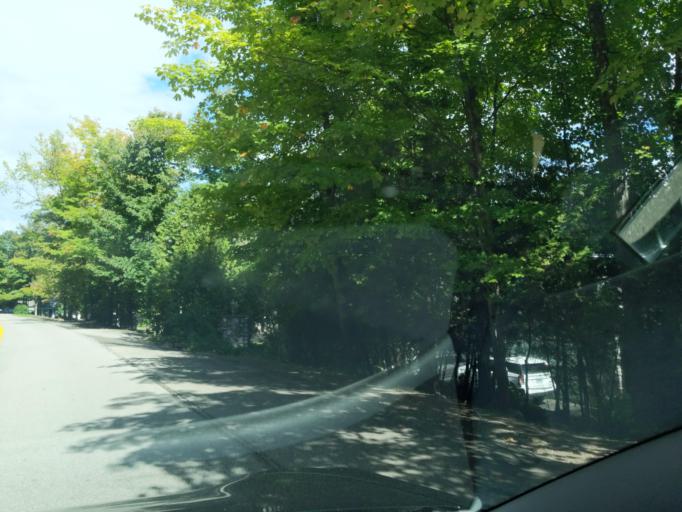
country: US
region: Michigan
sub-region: Antrim County
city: Bellaire
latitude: 44.9660
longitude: -85.3227
